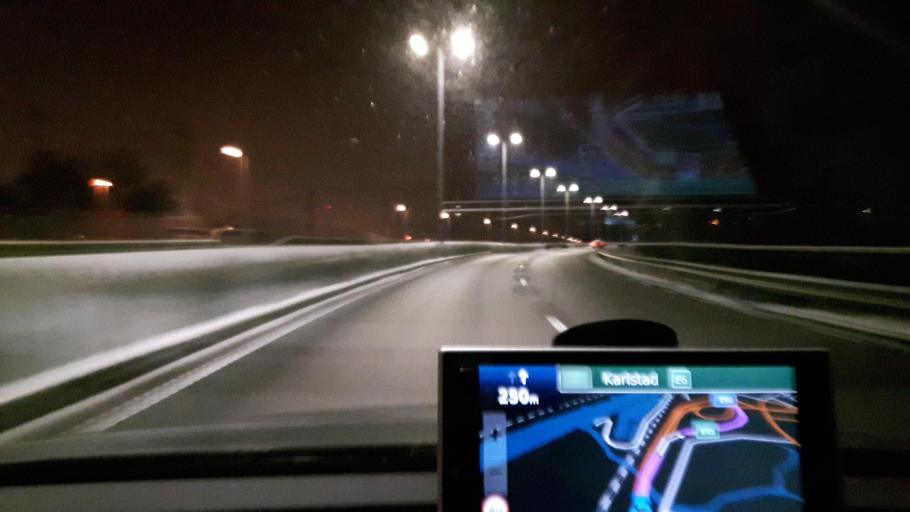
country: SE
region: Vaestra Goetaland
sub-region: Goteborg
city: Hammarkullen
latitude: 57.7602
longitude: 12.0047
